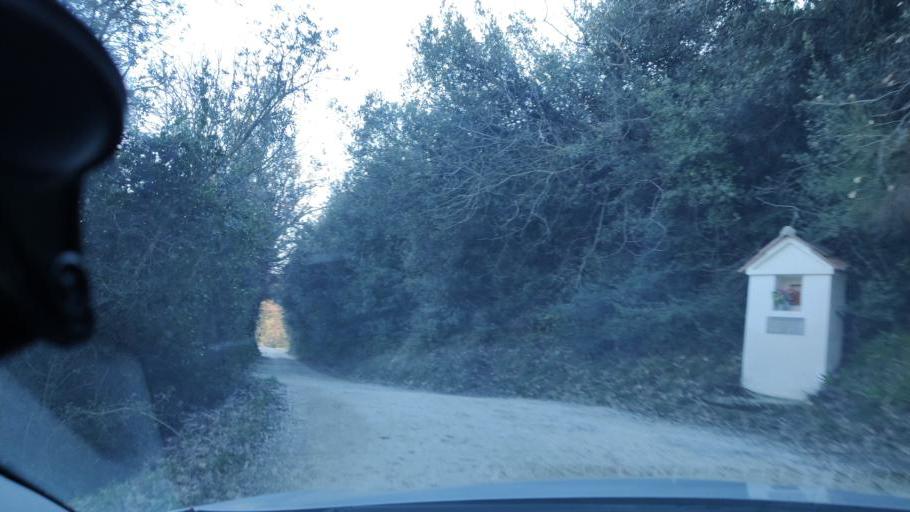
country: IT
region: Umbria
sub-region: Provincia di Terni
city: Fornole
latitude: 42.5544
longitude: 12.4448
